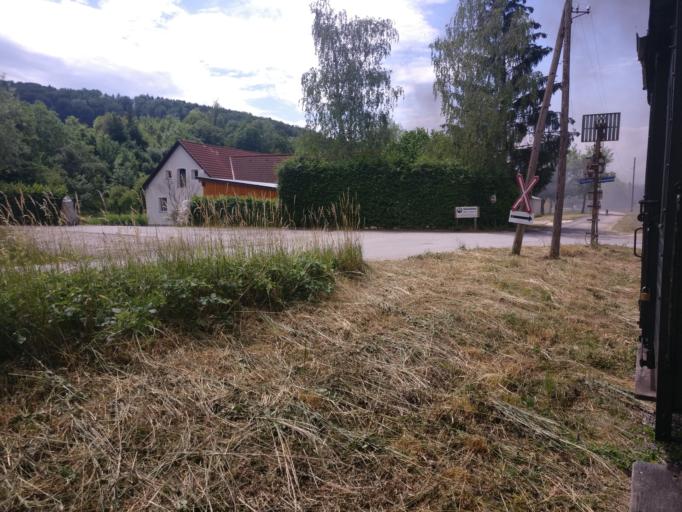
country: AT
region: Upper Austria
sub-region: Politischer Bezirk Steyr-Land
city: Sierning
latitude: 48.0186
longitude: 14.3201
